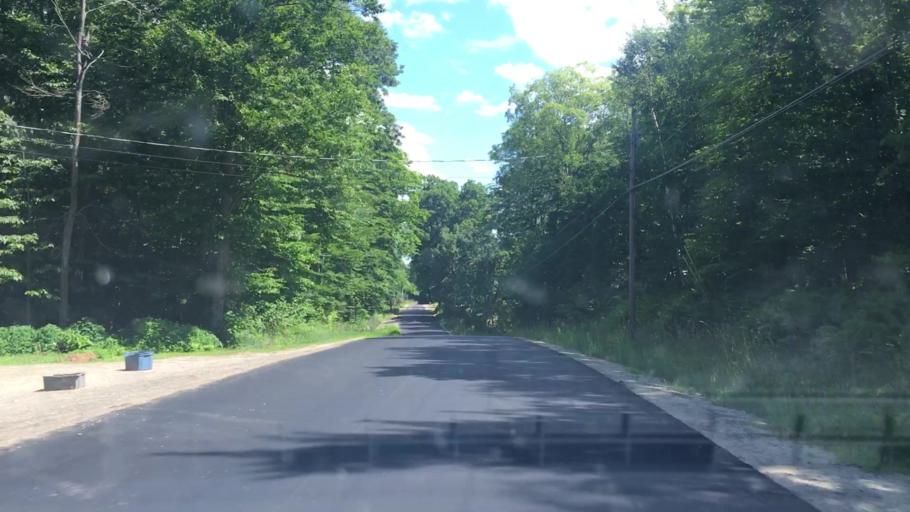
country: US
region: Maine
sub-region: Franklin County
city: Chesterville
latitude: 44.5698
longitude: -70.1489
